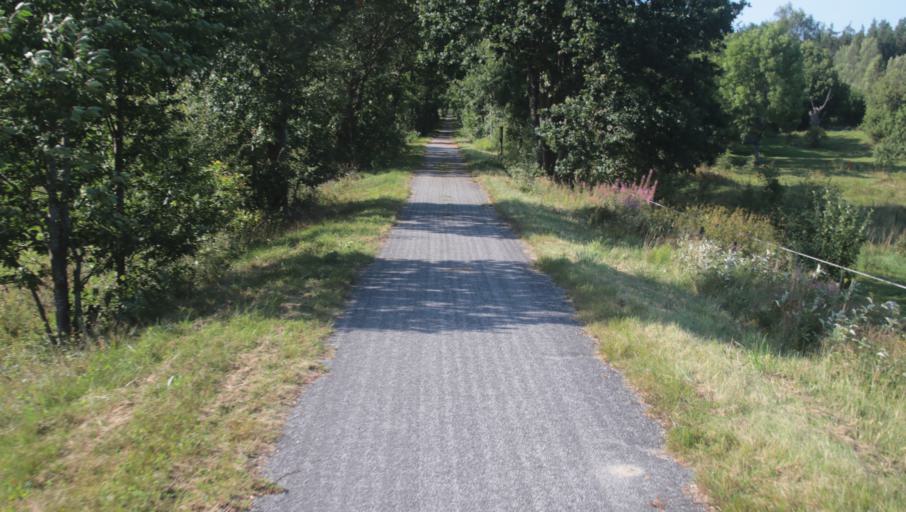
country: SE
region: Blekinge
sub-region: Karlshamns Kommun
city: Svangsta
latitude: 56.2999
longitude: 14.7333
